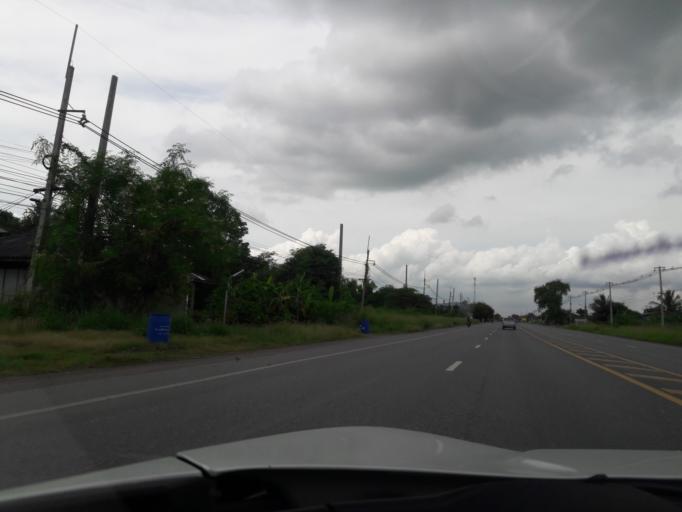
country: TH
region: Lop Buri
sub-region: Amphoe Tha Luang
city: Tha Luang
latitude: 15.0794
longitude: 101.0437
